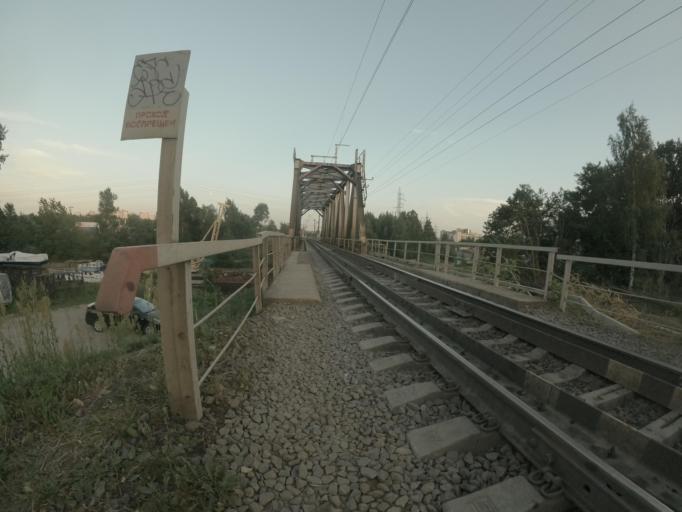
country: RU
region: St.-Petersburg
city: Krasnogvargeisky
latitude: 59.9419
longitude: 30.4479
